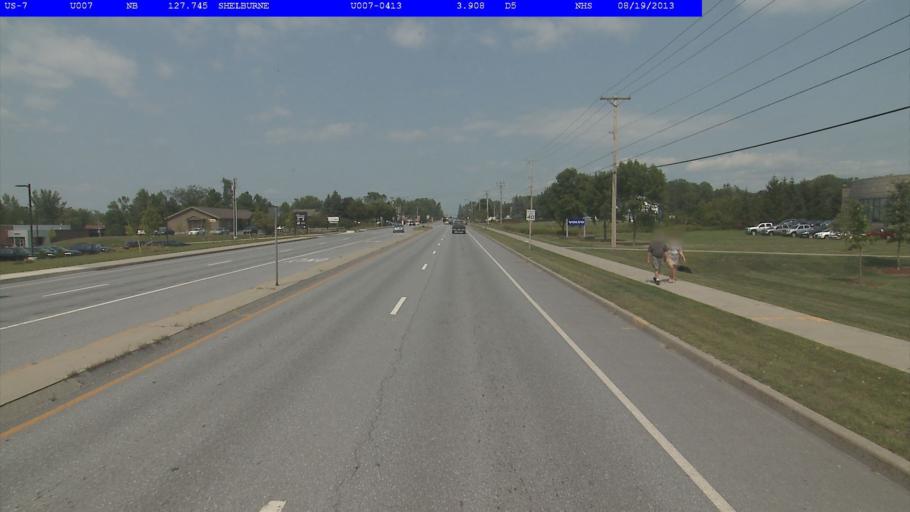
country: US
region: Vermont
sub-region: Chittenden County
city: Burlington
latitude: 44.4066
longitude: -73.2164
